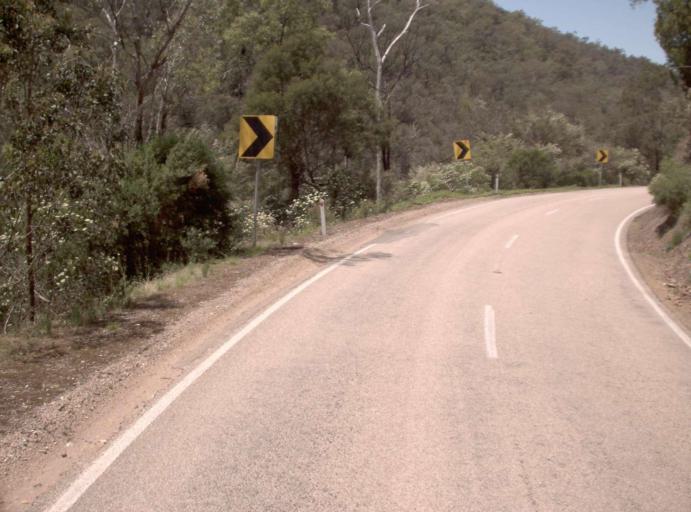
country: AU
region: Victoria
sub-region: East Gippsland
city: Lakes Entrance
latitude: -37.5346
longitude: 147.8628
